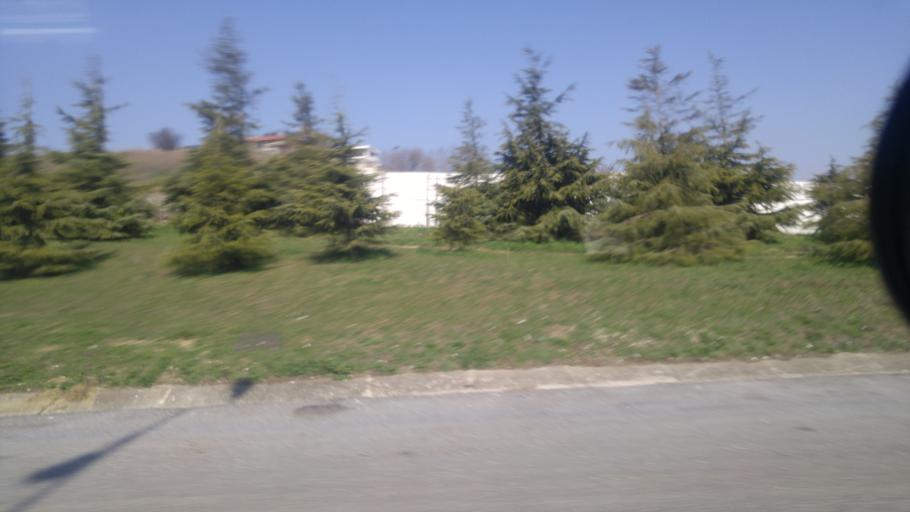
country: TR
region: Istanbul
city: Selimpasa
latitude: 41.0678
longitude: 28.3911
